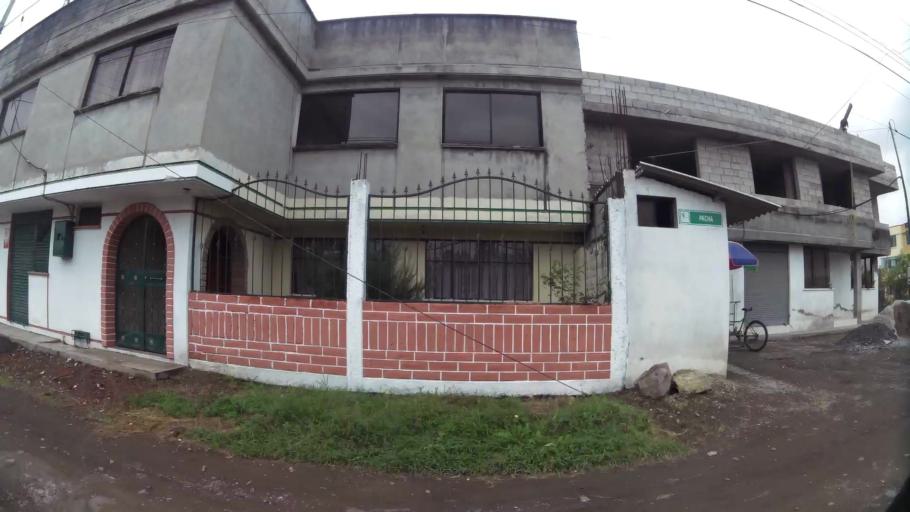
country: EC
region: Pichincha
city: Sangolqui
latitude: -0.3401
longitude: -78.4717
